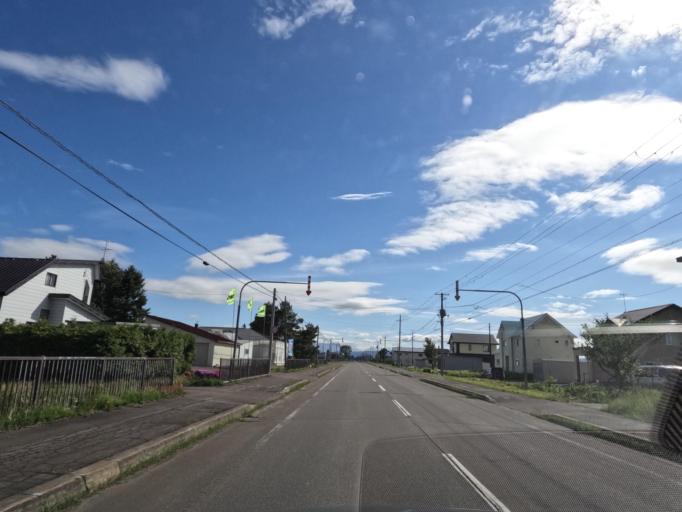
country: JP
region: Hokkaido
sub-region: Asahikawa-shi
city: Asahikawa
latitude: 43.7156
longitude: 142.5266
